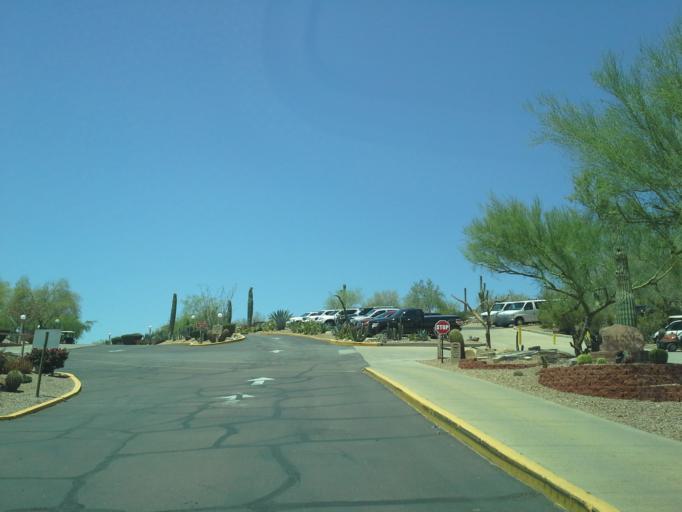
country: US
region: Arizona
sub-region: Pinal County
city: Apache Junction
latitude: 33.3614
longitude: -111.4446
